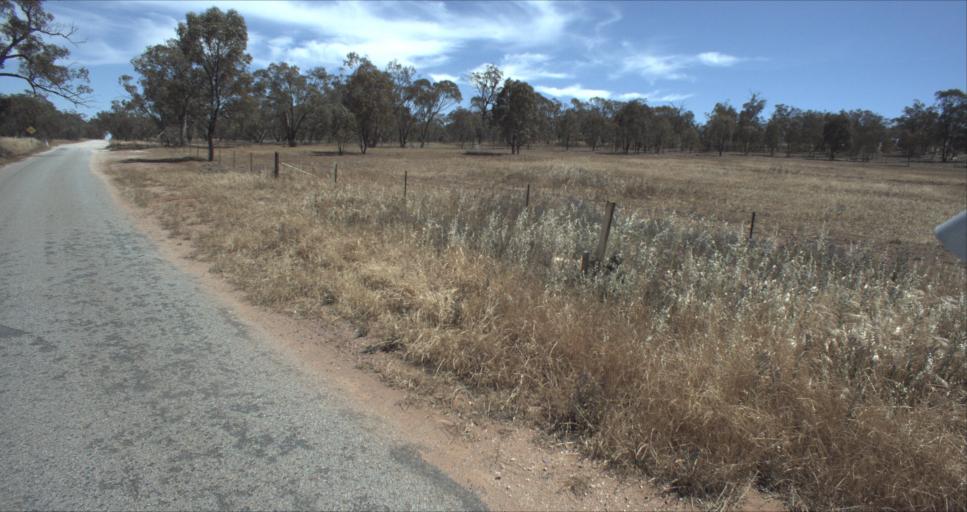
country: AU
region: New South Wales
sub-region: Leeton
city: Leeton
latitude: -34.6019
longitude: 146.4794
